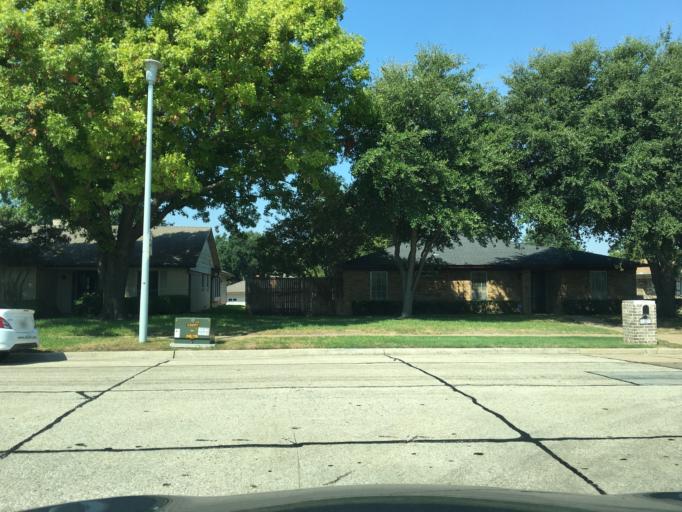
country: US
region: Texas
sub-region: Dallas County
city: Garland
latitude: 32.9373
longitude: -96.6569
